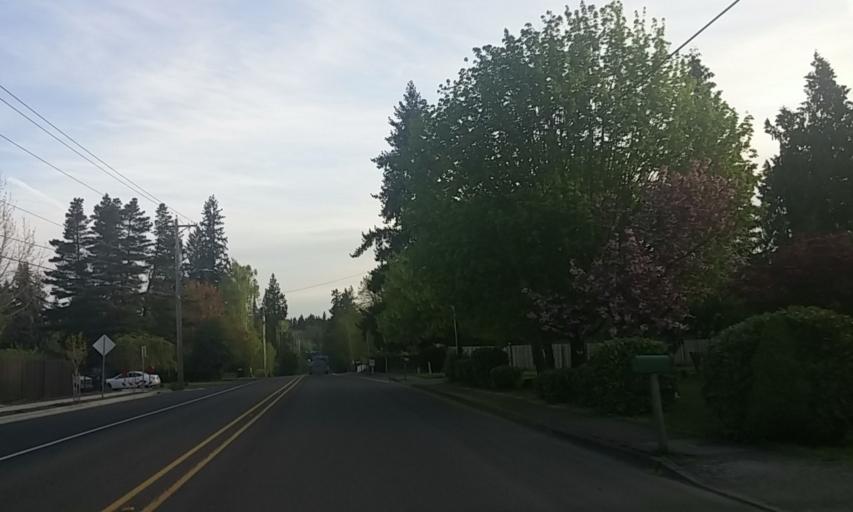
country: US
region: Oregon
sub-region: Washington County
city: Aloha
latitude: 45.5111
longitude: -122.8795
